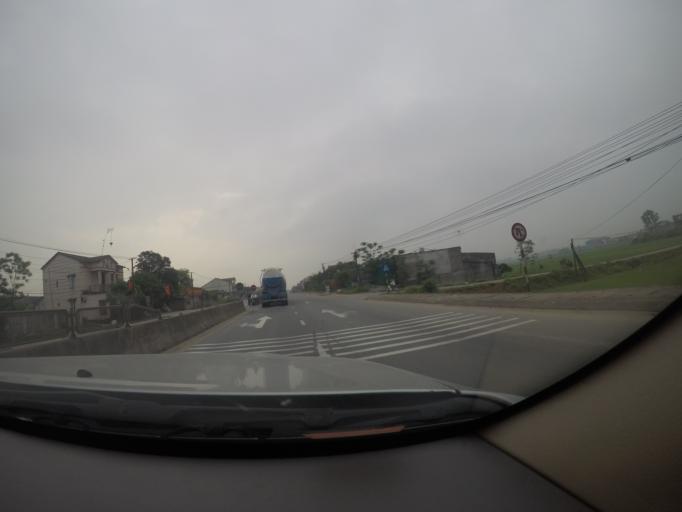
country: VN
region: Ha Tinh
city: Cam Xuyen
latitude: 18.1999
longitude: 106.1627
